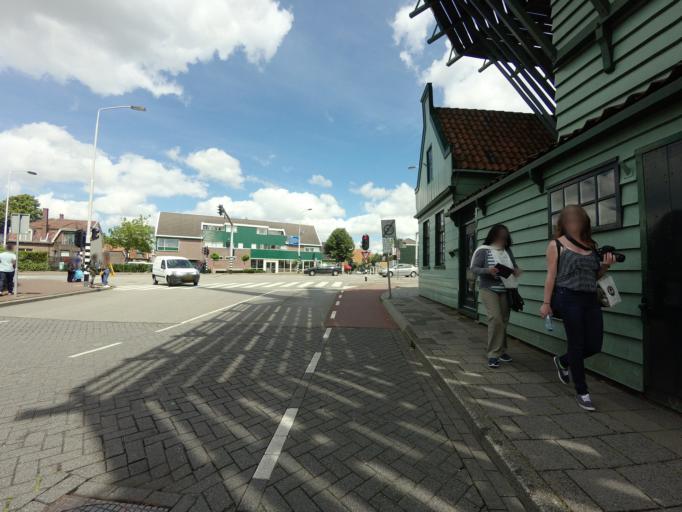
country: NL
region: North Holland
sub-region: Gemeente Zaanstad
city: Zaanstad
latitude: 52.4713
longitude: 4.8112
